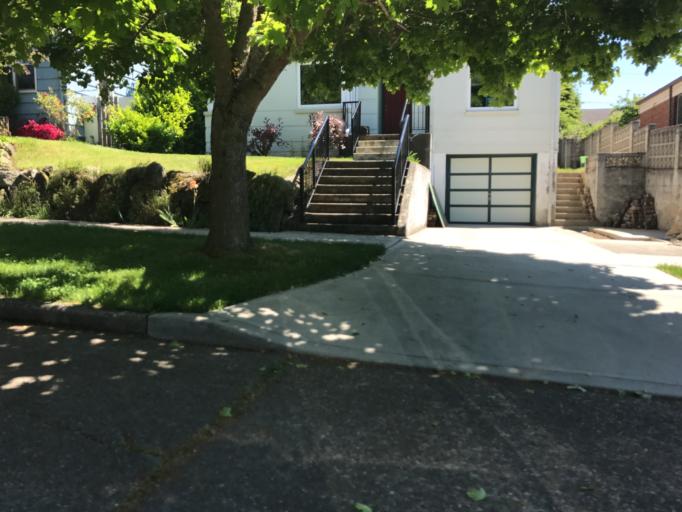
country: US
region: Washington
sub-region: King County
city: Seattle
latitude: 47.5850
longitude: -122.2951
